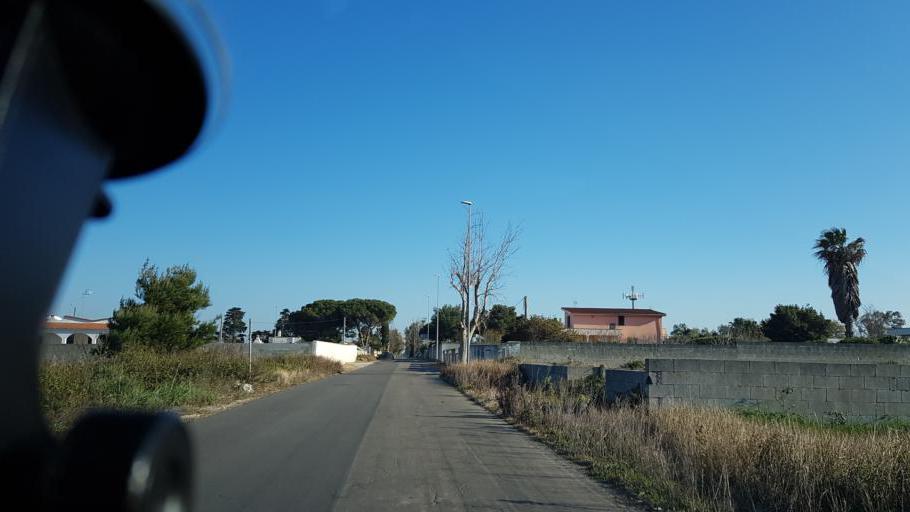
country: IT
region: Apulia
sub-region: Provincia di Lecce
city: Merine
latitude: 40.4264
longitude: 18.2441
